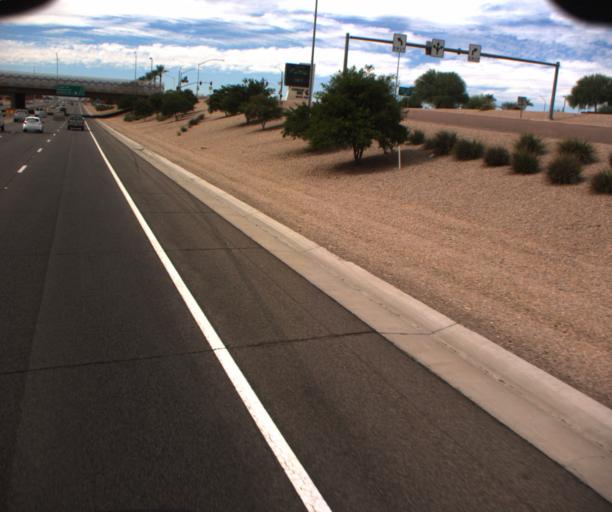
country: US
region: Arizona
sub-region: Maricopa County
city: Chandler
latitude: 33.2831
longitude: -111.7876
